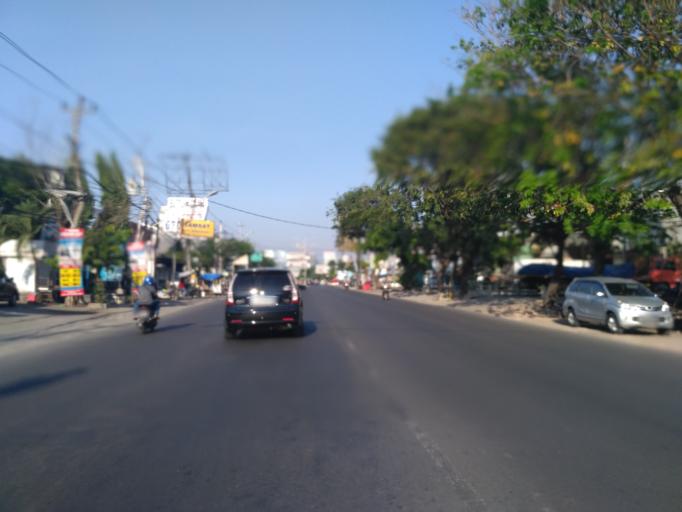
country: ID
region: Central Java
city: Mranggen
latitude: -7.0103
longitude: 110.4700
